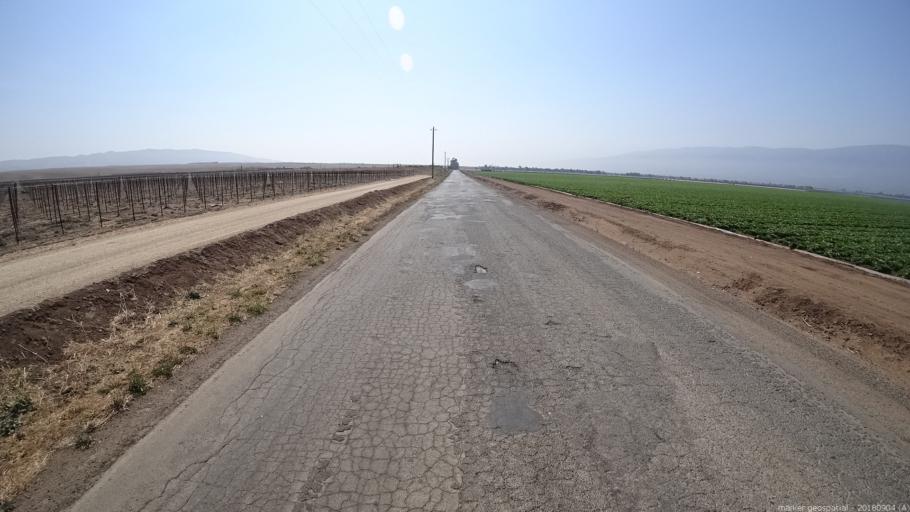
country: US
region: California
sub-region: Monterey County
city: Gonzales
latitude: 36.5248
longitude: -121.4167
